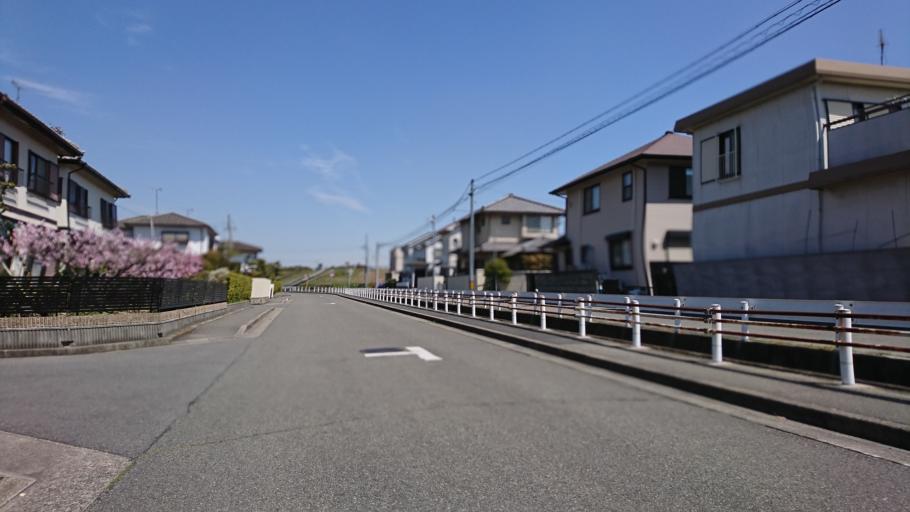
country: JP
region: Hyogo
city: Kakogawacho-honmachi
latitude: 34.7493
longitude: 134.8765
